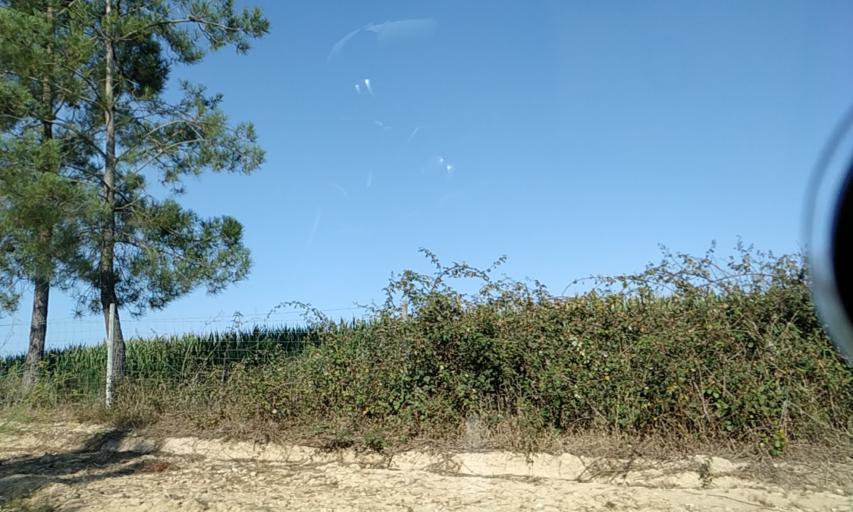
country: PT
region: Santarem
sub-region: Coruche
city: Coruche
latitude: 39.0277
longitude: -8.5625
